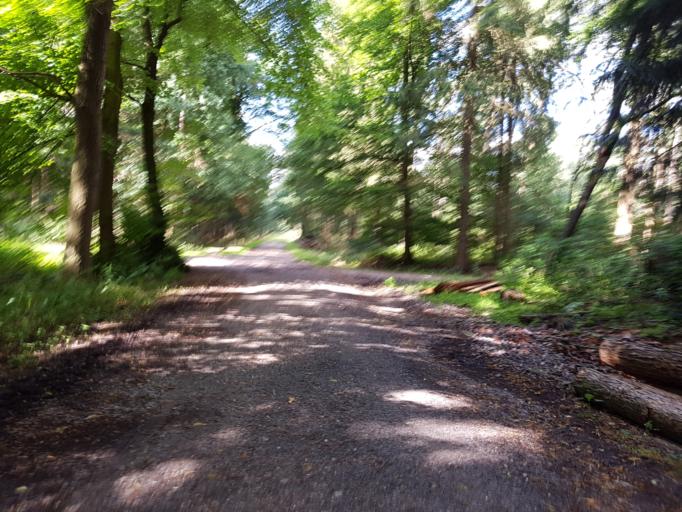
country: DE
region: Lower Saxony
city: Friedeburg
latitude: 53.4929
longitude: 7.8174
